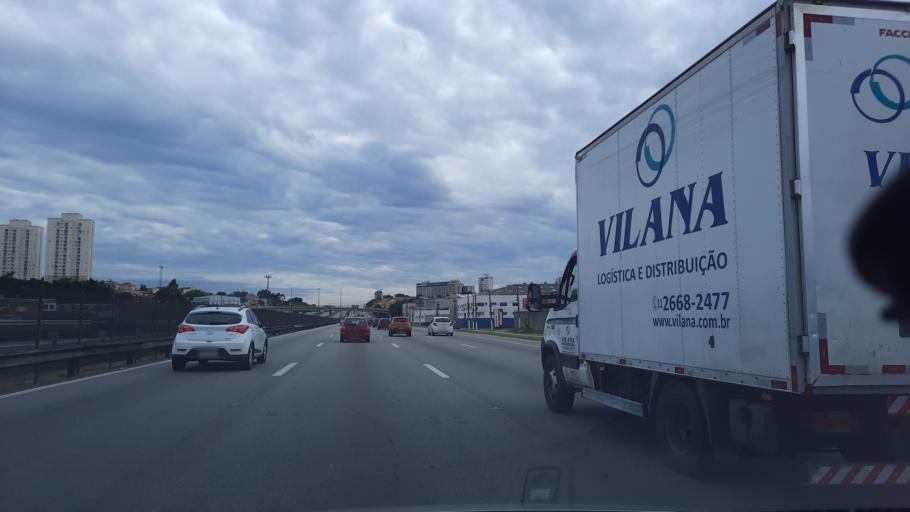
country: BR
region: Sao Paulo
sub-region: Guarulhos
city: Guarulhos
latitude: -23.5135
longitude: -46.5758
